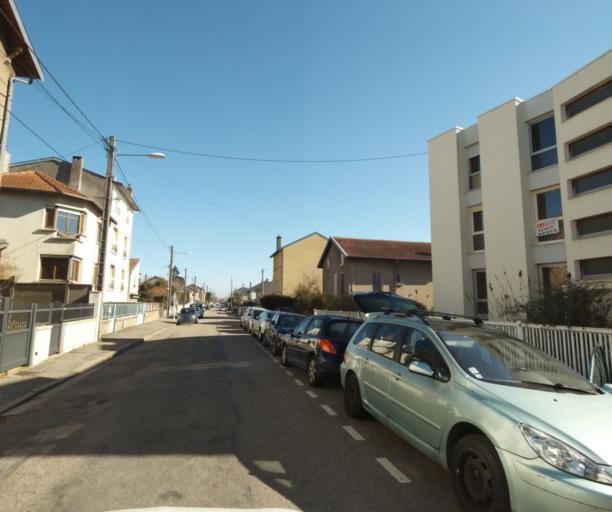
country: FR
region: Lorraine
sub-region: Departement de Meurthe-et-Moselle
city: Essey-les-Nancy
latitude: 48.7064
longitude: 6.2233
